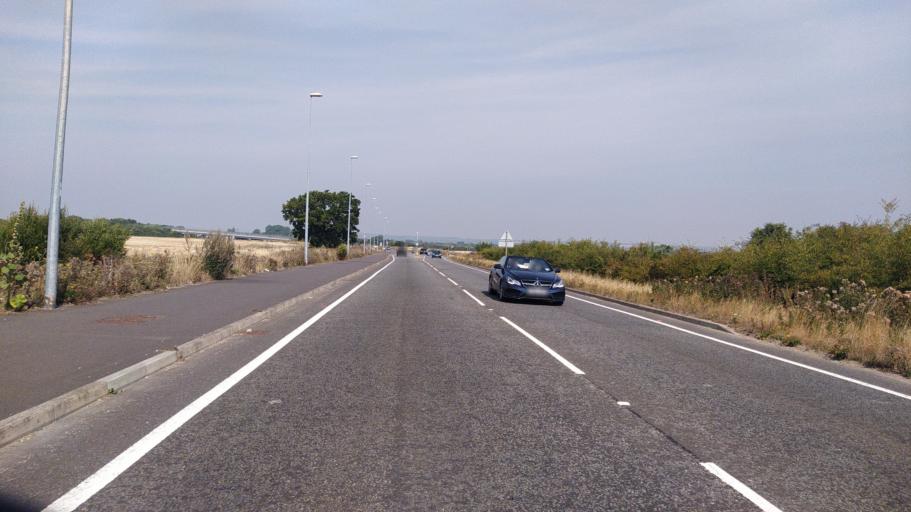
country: GB
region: England
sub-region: West Sussex
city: Barnham
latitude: 50.8057
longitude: -0.6479
